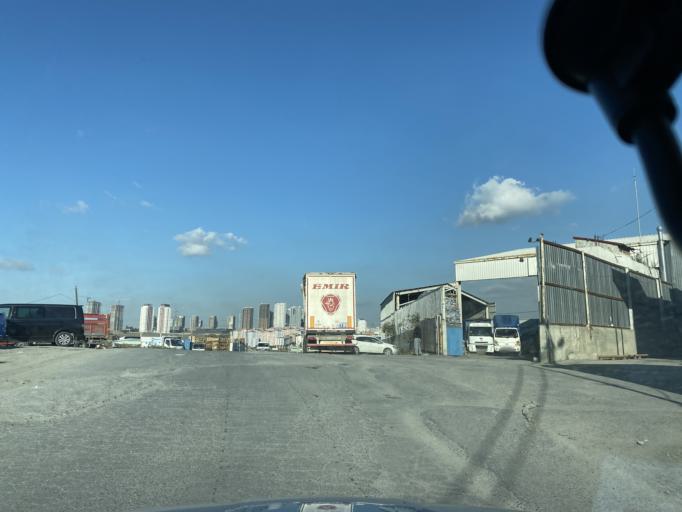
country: TR
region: Istanbul
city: Esenyurt
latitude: 41.0551
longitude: 28.6480
